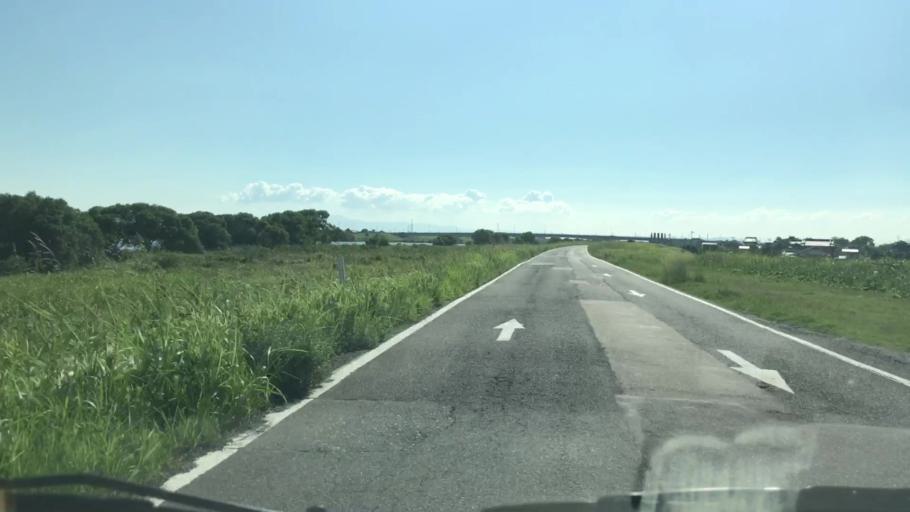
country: JP
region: Saga Prefecture
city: Kanzakimachi-kanzaki
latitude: 33.2750
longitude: 130.4415
